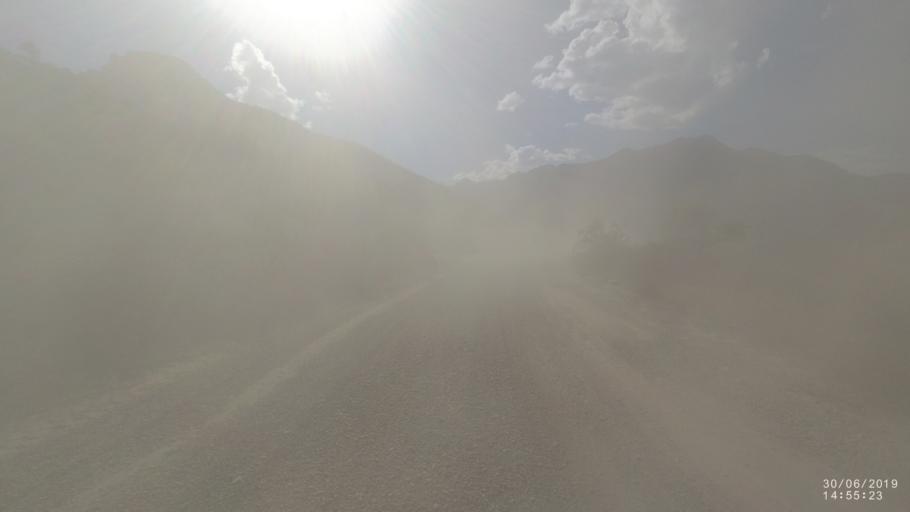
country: BO
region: Cochabamba
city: Irpa Irpa
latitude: -17.7545
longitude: -66.3525
